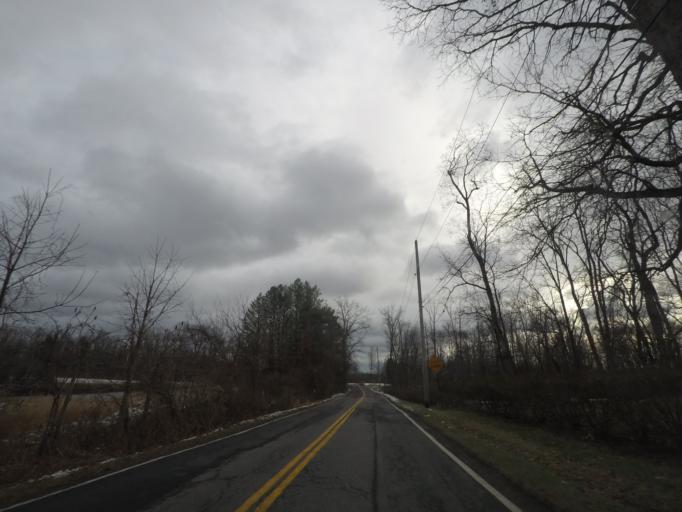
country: US
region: New York
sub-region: Rensselaer County
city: East Greenbush
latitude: 42.5858
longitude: -73.7194
